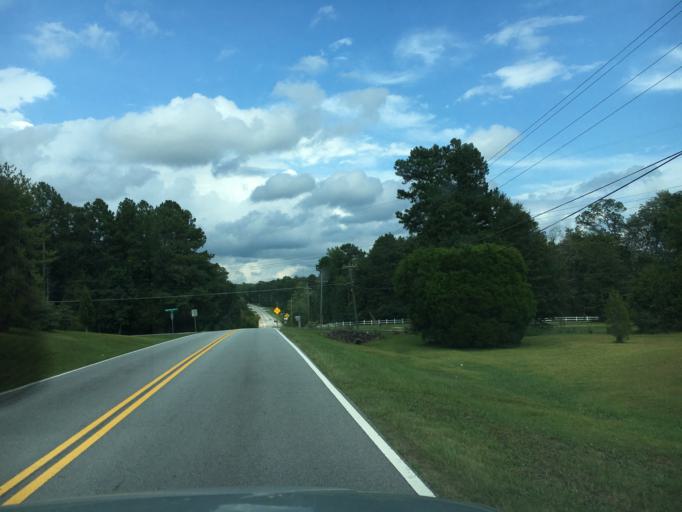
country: US
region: Georgia
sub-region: Rockdale County
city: Lakeview Estates
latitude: 33.7770
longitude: -83.9839
